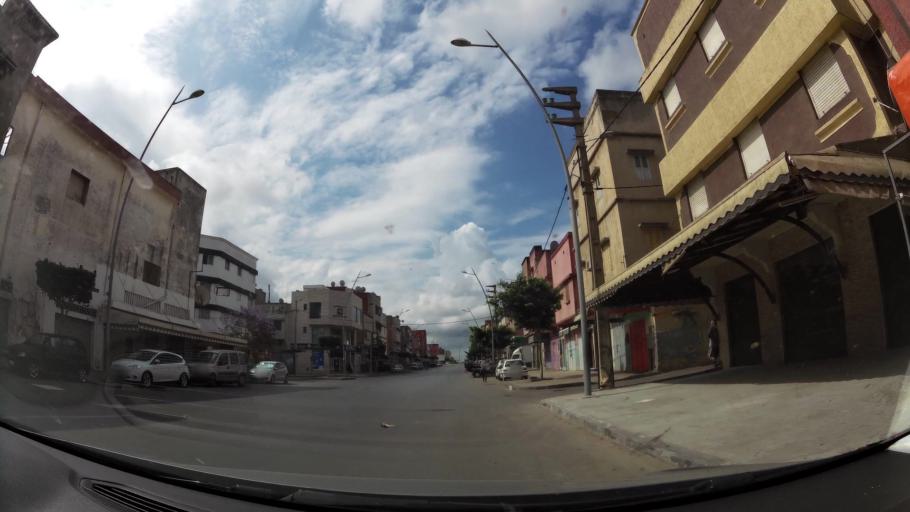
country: MA
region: Gharb-Chrarda-Beni Hssen
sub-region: Kenitra Province
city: Kenitra
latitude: 34.2622
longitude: -6.5598
